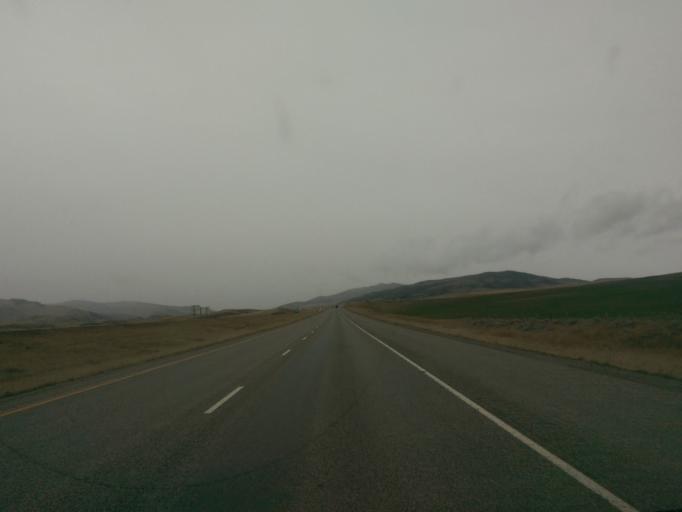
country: US
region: Montana
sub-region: Gallatin County
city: Three Forks
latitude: 45.9134
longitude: -111.7636
